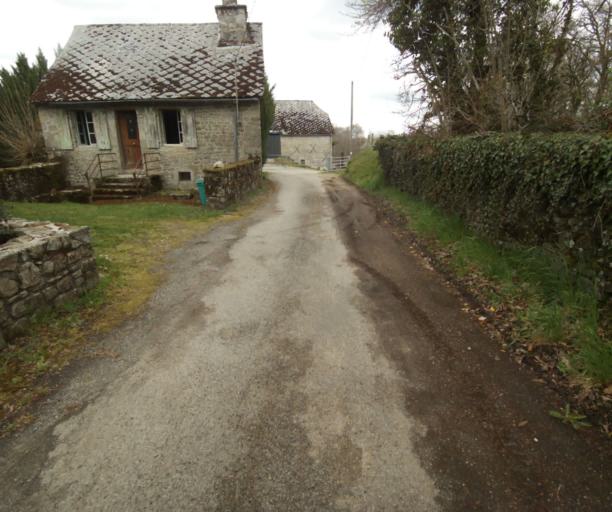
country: FR
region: Limousin
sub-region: Departement de la Correze
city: Argentat
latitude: 45.2130
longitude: 1.9108
